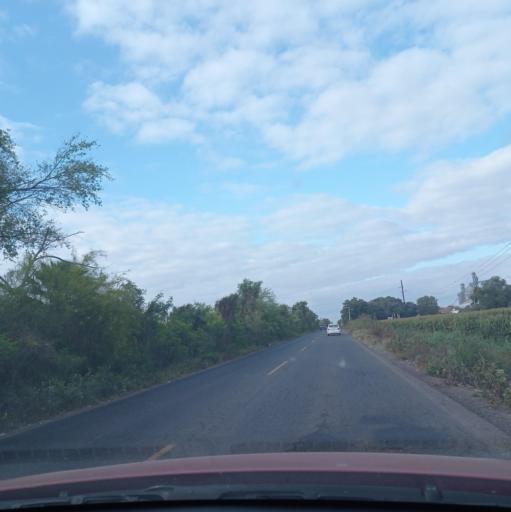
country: MX
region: Sinaloa
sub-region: Guasave
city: Las Quemazones
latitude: 25.6536
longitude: -108.5262
